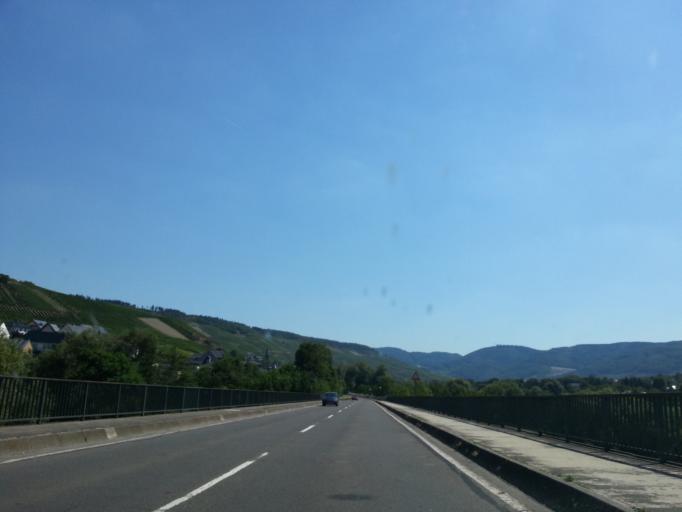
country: DE
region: Rheinland-Pfalz
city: Lieser
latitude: 49.9164
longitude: 7.0073
